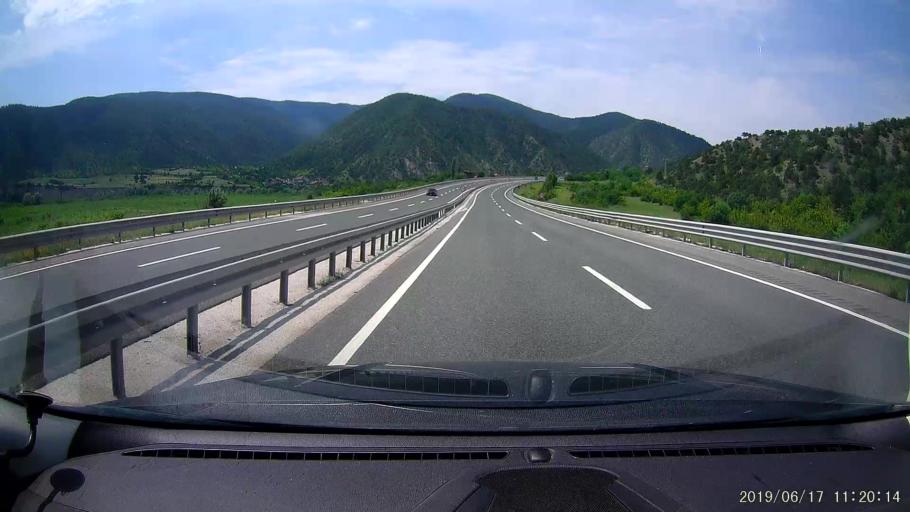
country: TR
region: Cankiri
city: Yaprakli
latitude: 40.9156
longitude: 33.8119
